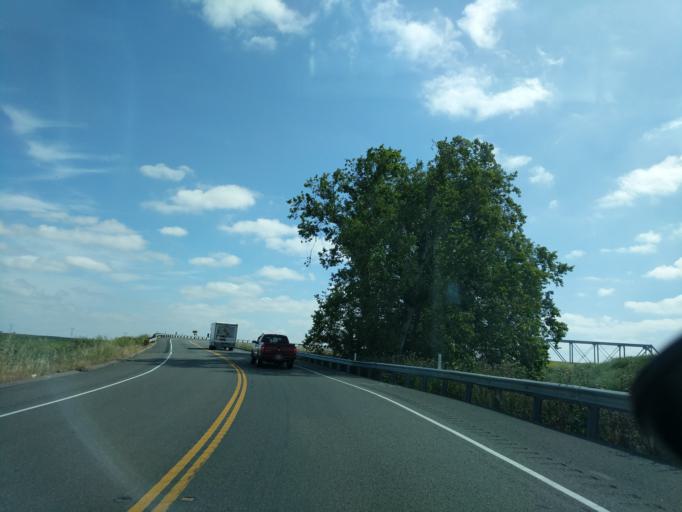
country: US
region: California
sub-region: Contra Costa County
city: Discovery Bay
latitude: 37.8906
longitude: -121.5738
